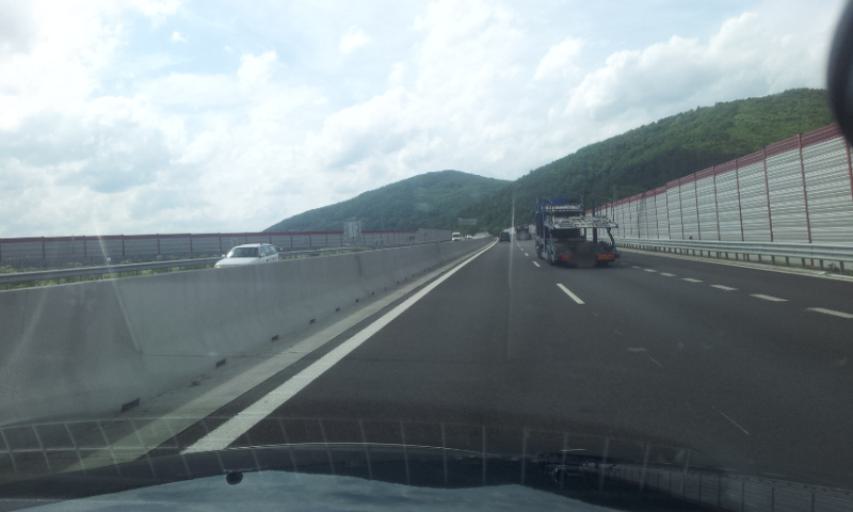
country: SK
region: Banskobystricky
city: Detva
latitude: 48.5382
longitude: 19.3991
